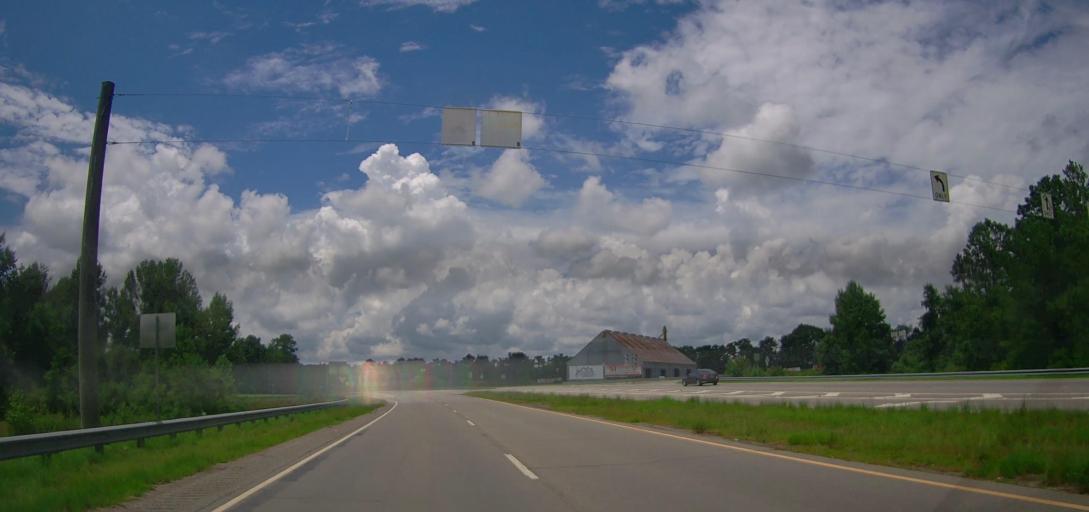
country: US
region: Georgia
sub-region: Dodge County
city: Eastman
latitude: 32.1946
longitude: -83.2087
